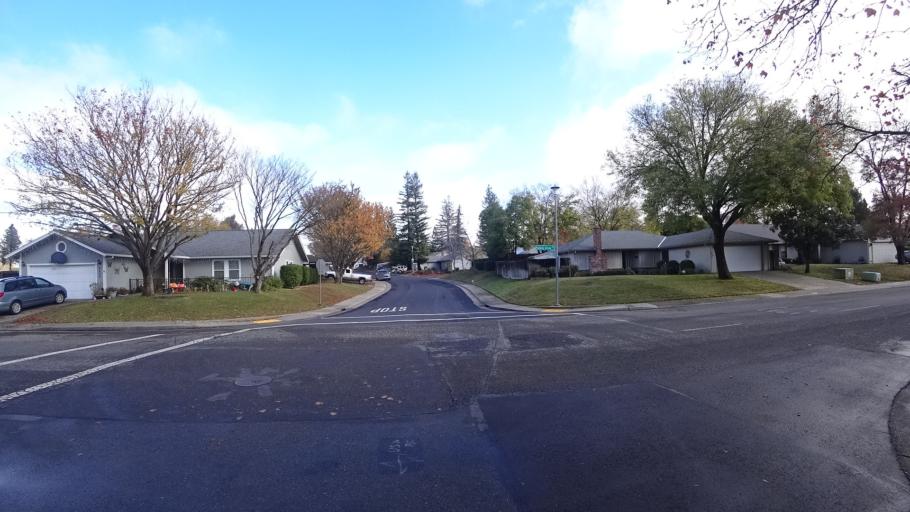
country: US
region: California
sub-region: Sacramento County
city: Antelope
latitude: 38.6898
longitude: -121.3248
